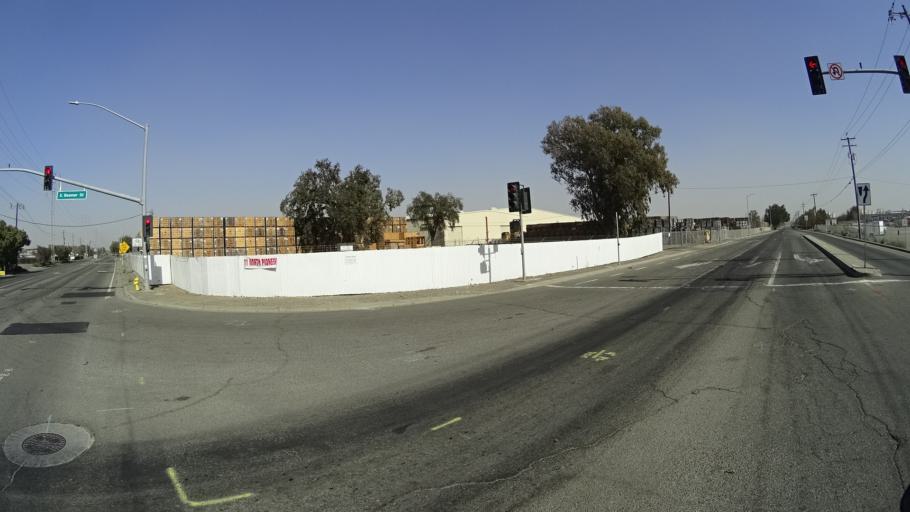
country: US
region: California
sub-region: Yolo County
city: Woodland
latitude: 38.6845
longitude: -121.7468
